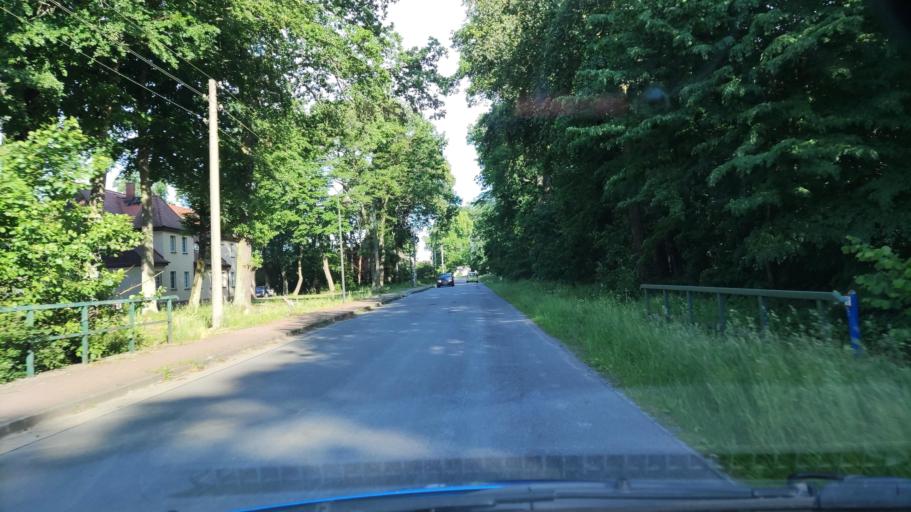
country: DE
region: Saxony-Anhalt
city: Letzlingen
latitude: 52.4489
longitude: 11.4798
